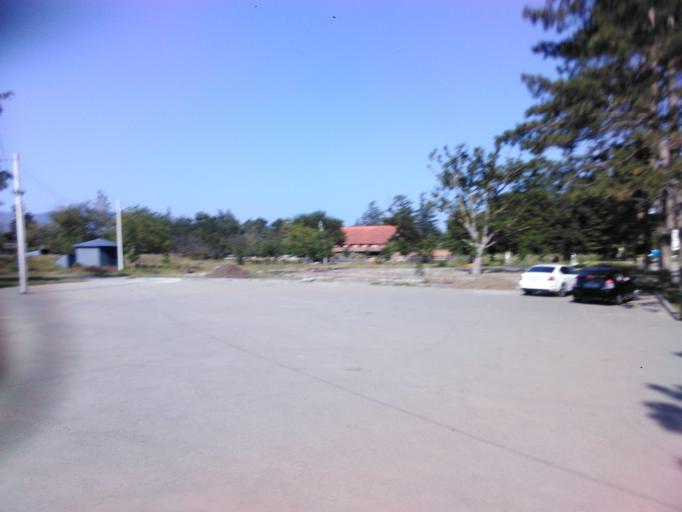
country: GE
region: Shida Kartli
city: Kaspi
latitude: 41.9422
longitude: 44.5824
